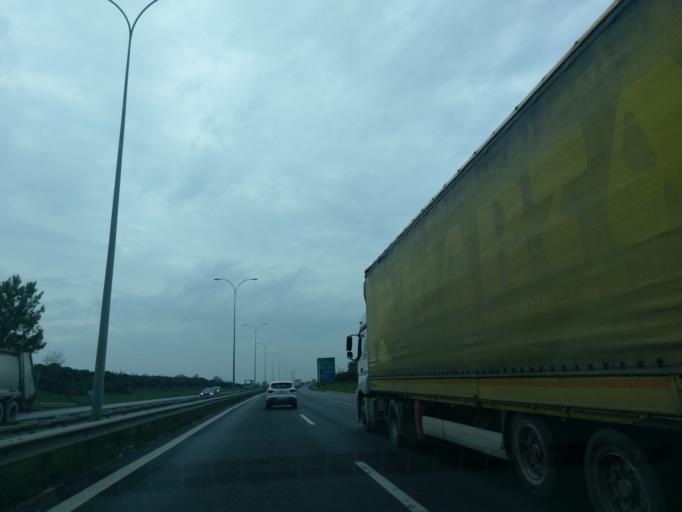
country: TR
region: Istanbul
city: Silivri
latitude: 41.1192
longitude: 28.2134
